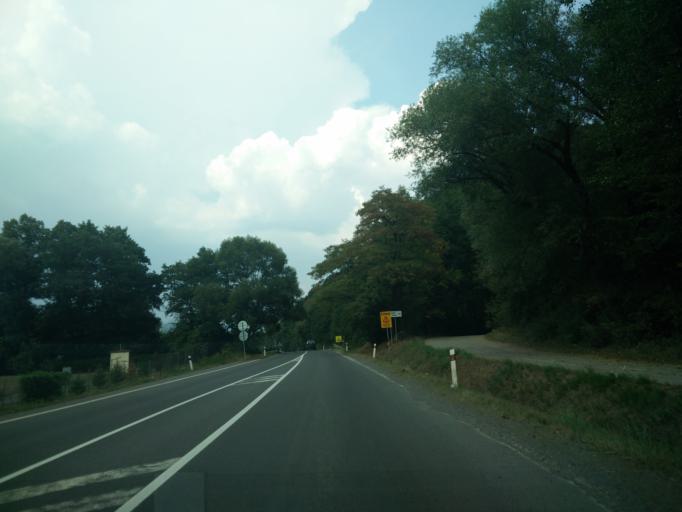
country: SK
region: Banskobystricky
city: Zarnovica
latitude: 48.5167
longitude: 18.7398
